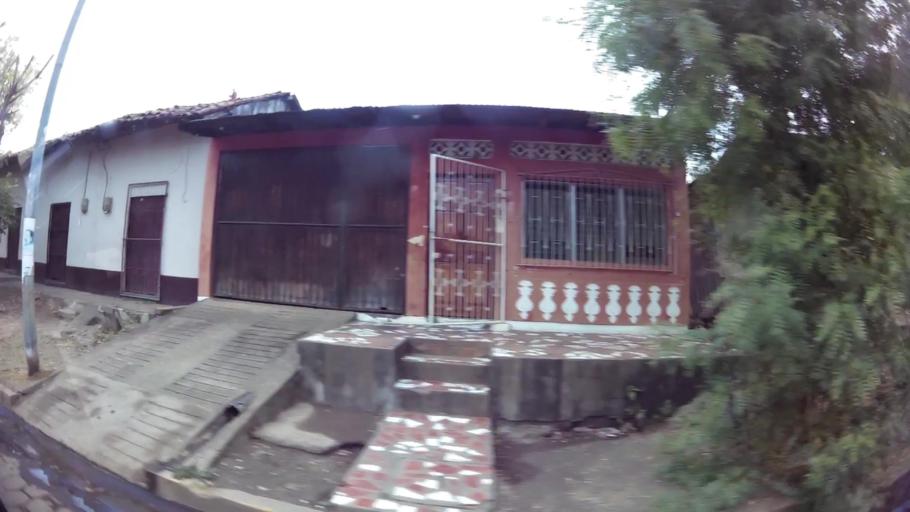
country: NI
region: Leon
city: Leon
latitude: 12.4285
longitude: -86.8753
